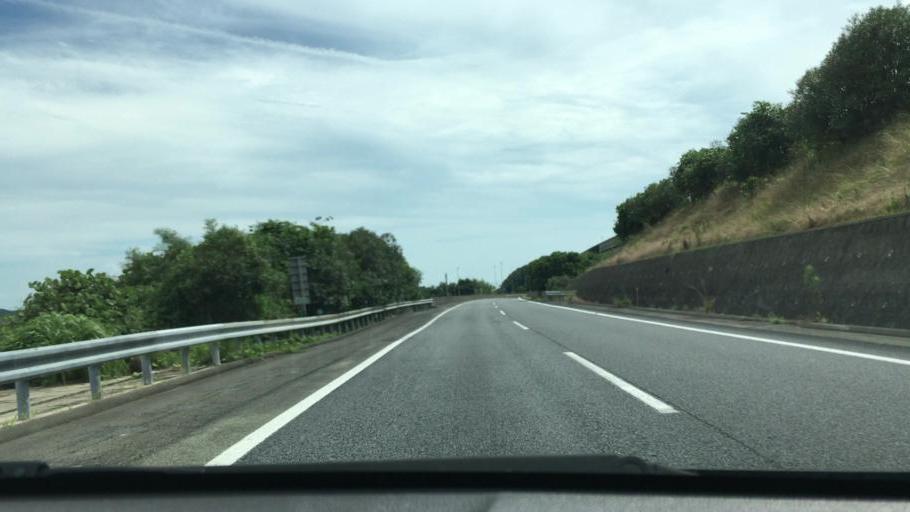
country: JP
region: Yamaguchi
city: Hofu
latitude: 34.0632
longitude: 131.6548
